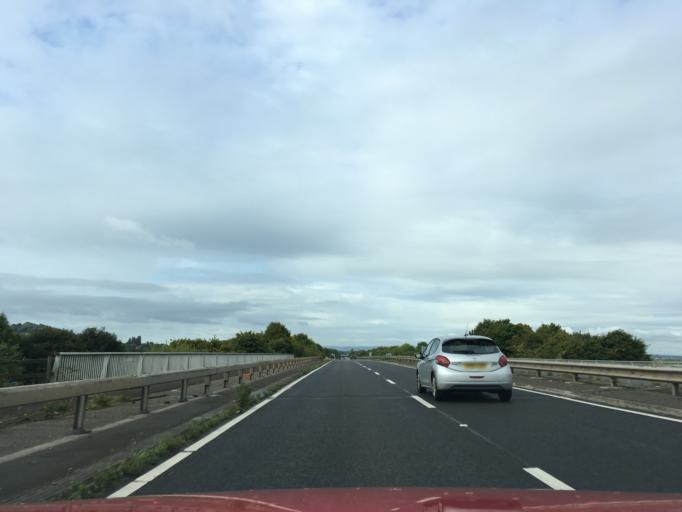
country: GB
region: England
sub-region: Gloucestershire
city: Churchdown
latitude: 51.8894
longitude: -2.1521
